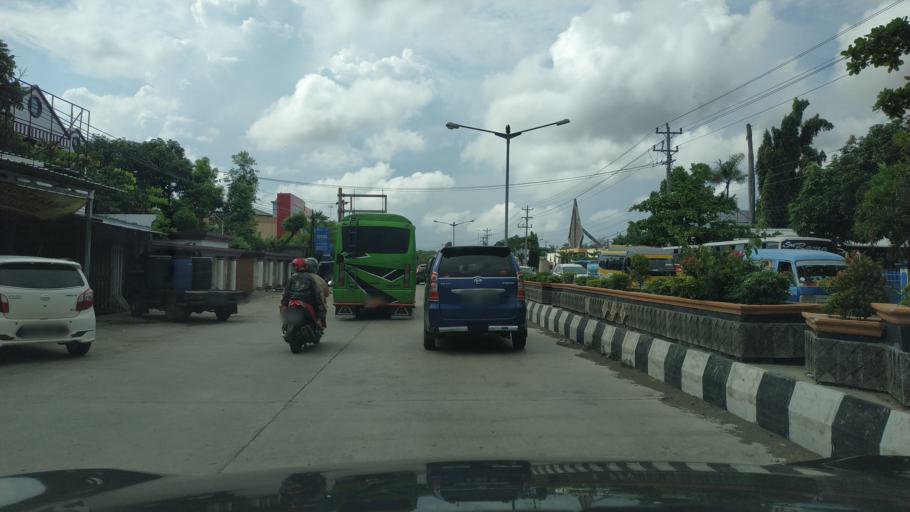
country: ID
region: Central Java
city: Pemalang
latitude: -6.9063
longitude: 109.3831
